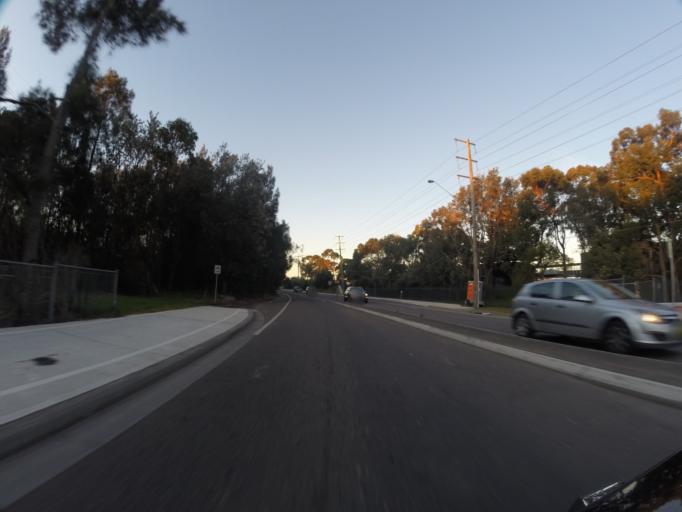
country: AU
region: New South Wales
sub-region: Sutherland Shire
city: Cronulla
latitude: -34.0389
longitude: 151.1570
